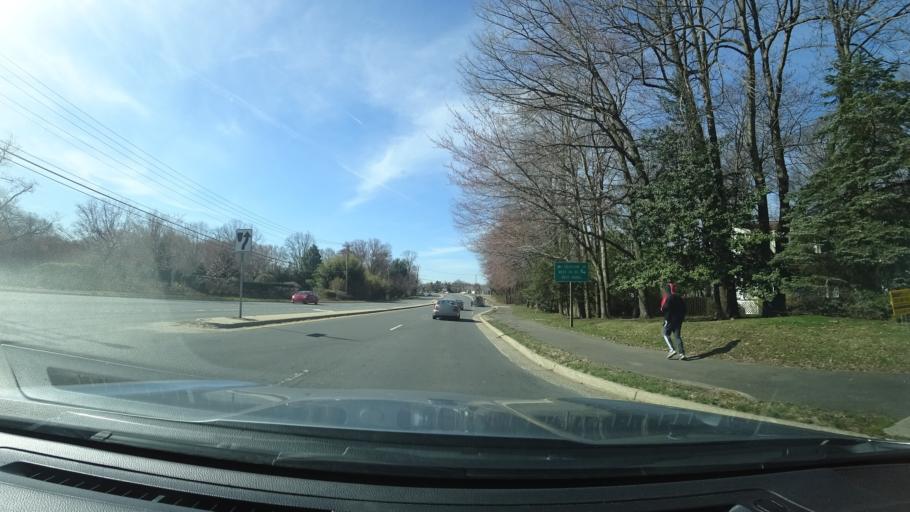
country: US
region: Virginia
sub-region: Fairfax County
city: Oak Hill
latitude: 38.9119
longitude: -77.3796
